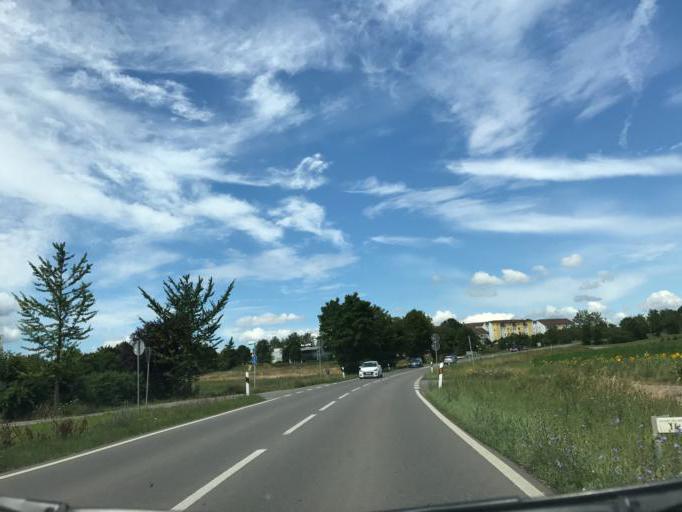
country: DE
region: Baden-Wuerttemberg
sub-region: Regierungsbezirk Stuttgart
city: Waiblingen
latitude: 48.8050
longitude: 9.3306
